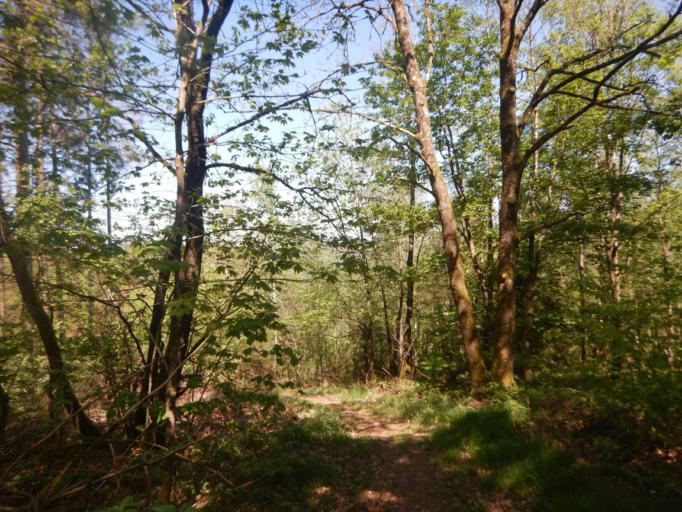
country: LU
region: Diekirch
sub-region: Canton de Diekirch
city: Bourscheid
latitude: 49.8978
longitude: 6.0718
